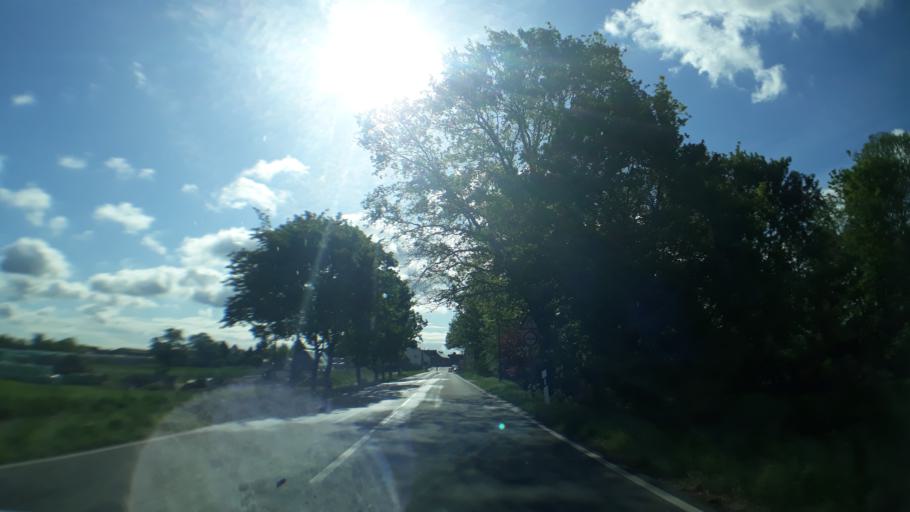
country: DE
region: North Rhine-Westphalia
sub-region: Regierungsbezirk Koln
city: Euskirchen
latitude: 50.6644
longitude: 6.7331
